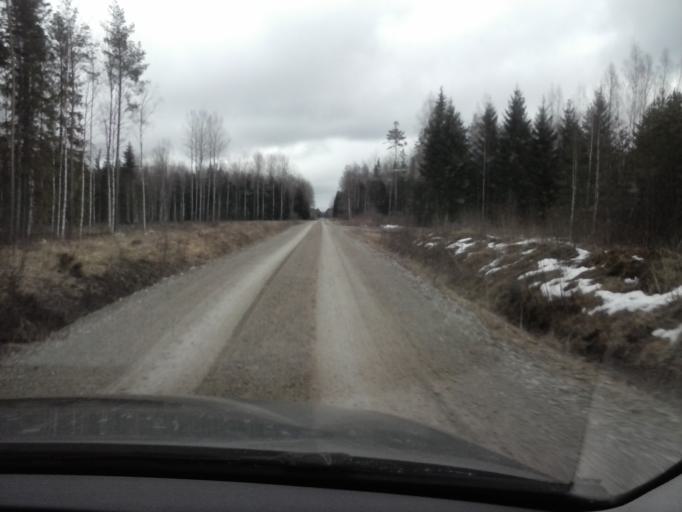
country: EE
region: Jogevamaa
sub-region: Mustvee linn
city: Mustvee
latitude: 59.0588
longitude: 26.8223
